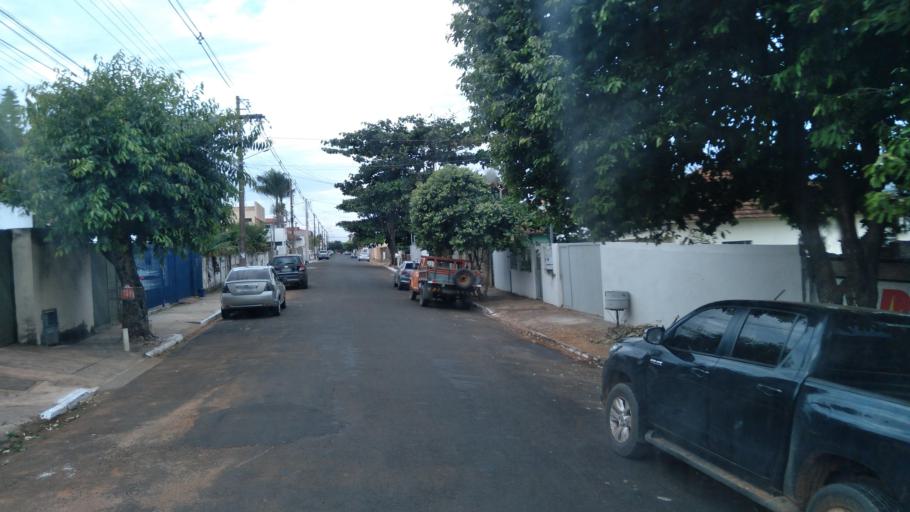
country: BR
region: Goias
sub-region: Mineiros
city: Mineiros
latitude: -17.5683
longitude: -52.5587
